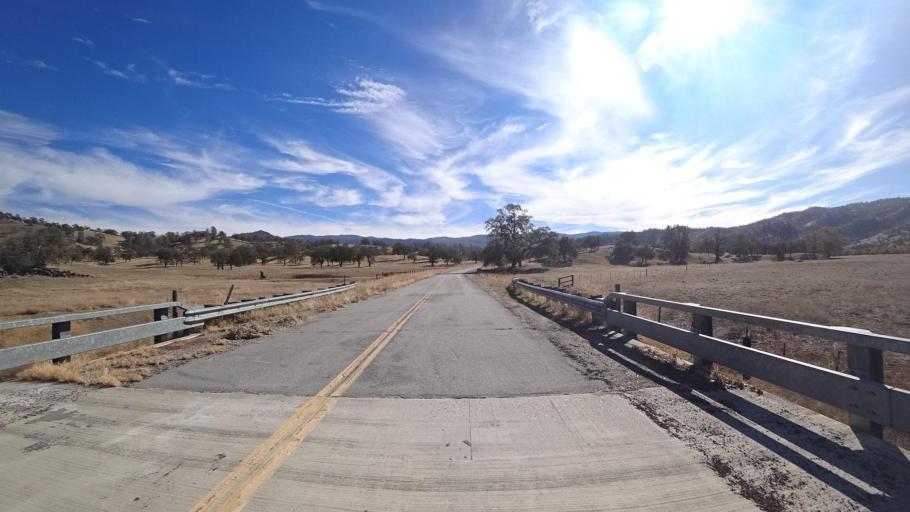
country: US
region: California
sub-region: Kern County
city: Alta Sierra
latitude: 35.6263
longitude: -118.7484
